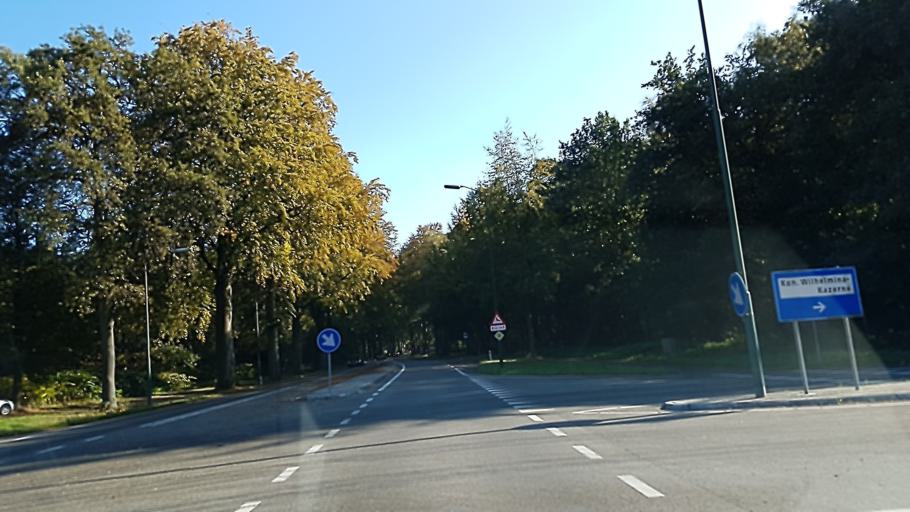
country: BE
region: Flanders
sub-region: Provincie Antwerpen
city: Stabroek
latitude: 51.3830
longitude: 4.3725
